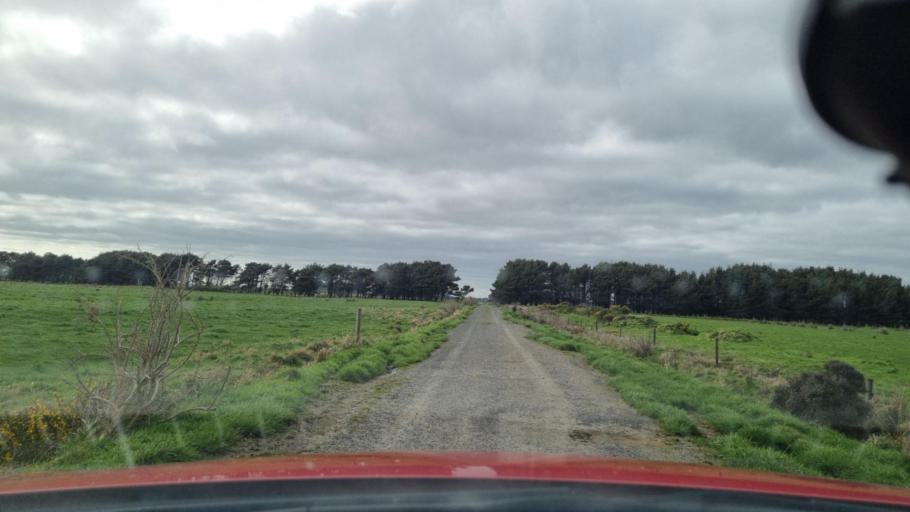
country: NZ
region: Southland
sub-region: Invercargill City
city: Bluff
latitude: -46.5157
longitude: 168.2999
